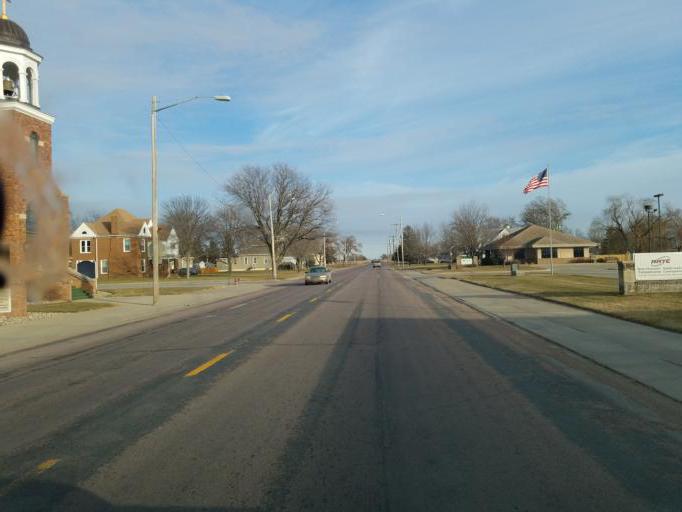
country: US
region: South Dakota
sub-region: Union County
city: Dakota Dunes
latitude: 42.4483
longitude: -96.5646
